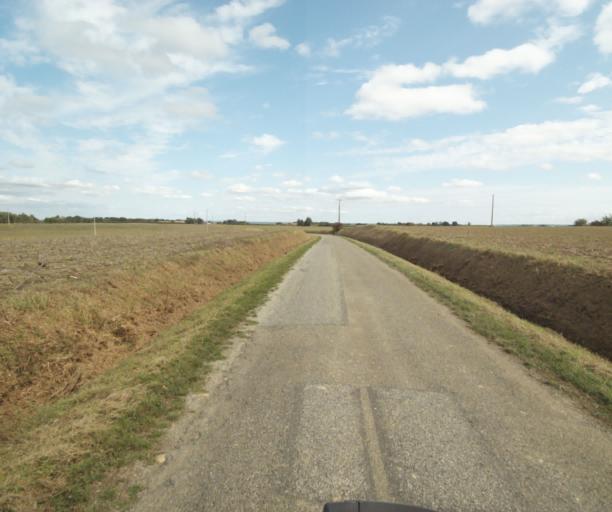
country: FR
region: Midi-Pyrenees
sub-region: Departement du Tarn-et-Garonne
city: Finhan
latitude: 43.8786
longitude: 1.1745
